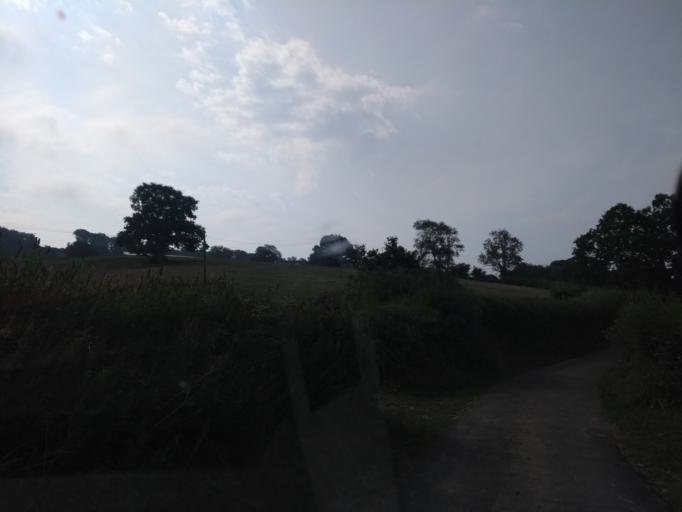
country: GB
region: England
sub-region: Somerset
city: Chard
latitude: 50.8850
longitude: -3.0443
